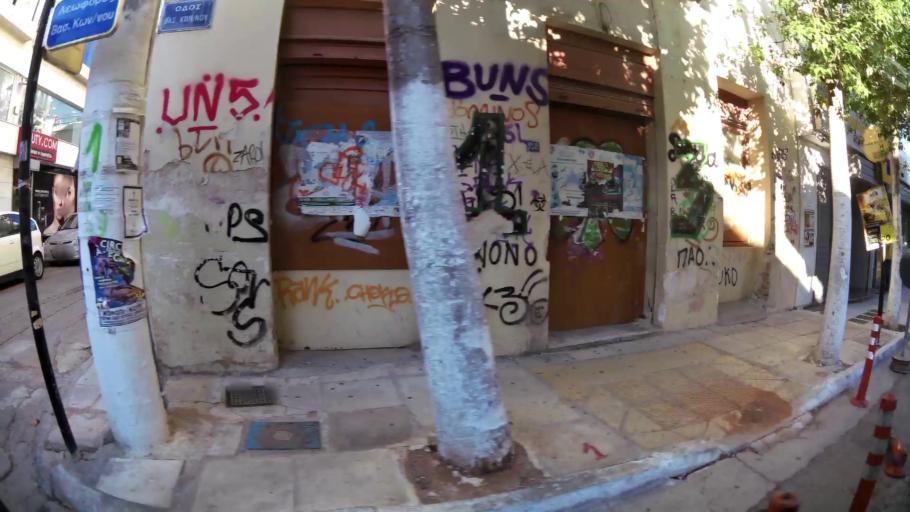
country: GR
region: Attica
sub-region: Nomarchia Anatolikis Attikis
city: Koropi
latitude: 37.9012
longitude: 23.8725
